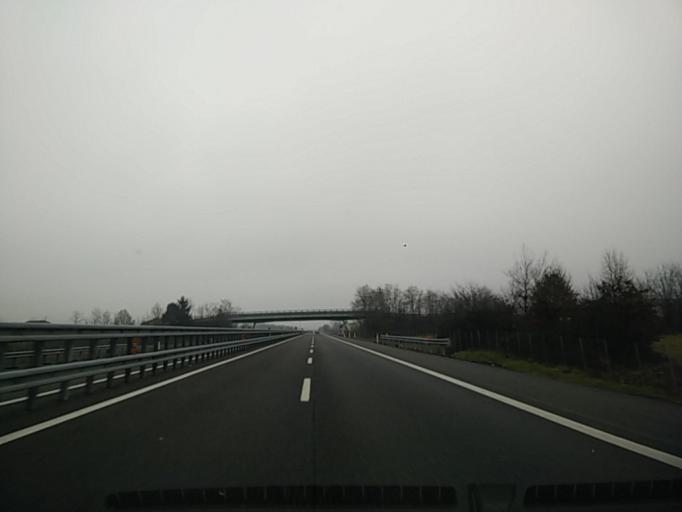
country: IT
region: Piedmont
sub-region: Provincia di Asti
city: Villafranca d'Asti
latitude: 44.9234
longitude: 8.0190
